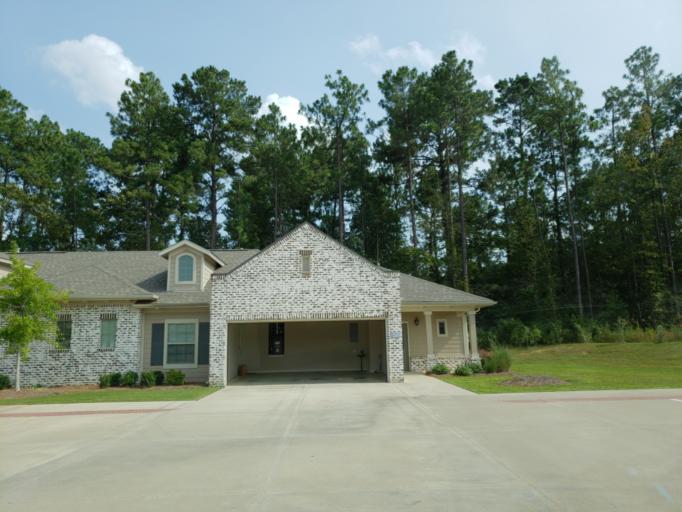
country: US
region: Mississippi
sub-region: Forrest County
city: Hattiesburg
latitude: 31.2751
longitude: -89.3250
